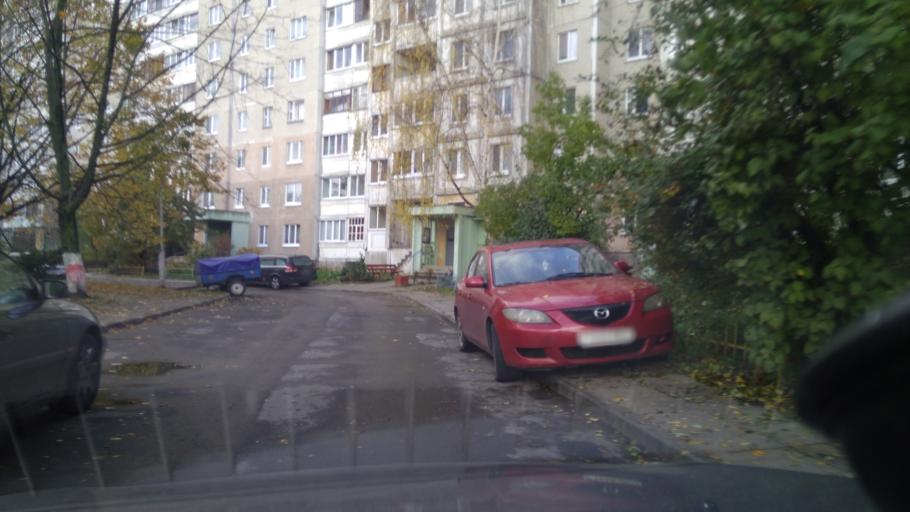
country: BY
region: Minsk
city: Malinovka
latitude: 53.8569
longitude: 27.4351
